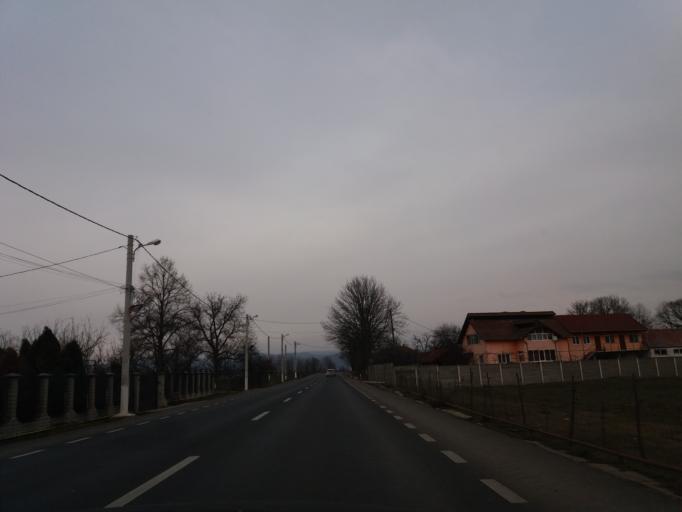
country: RO
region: Hunedoara
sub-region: Comuna Bacia
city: Bacia
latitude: 45.8059
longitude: 23.0137
